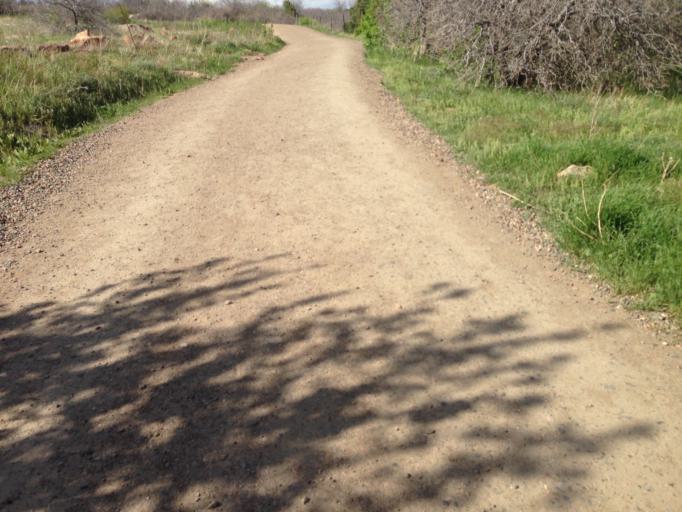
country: US
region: Colorado
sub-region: Boulder County
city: Boulder
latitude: 39.9407
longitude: -105.2602
